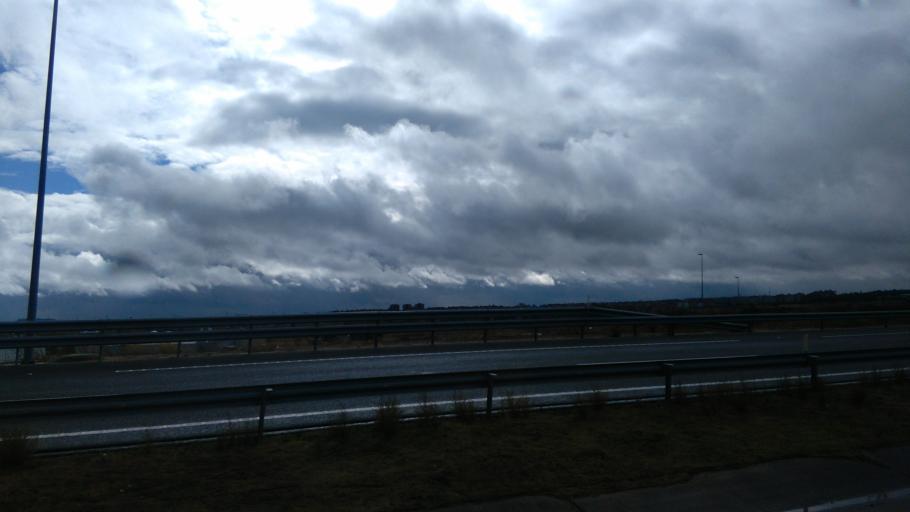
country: ES
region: Madrid
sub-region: Provincia de Madrid
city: Leganes
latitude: 40.3575
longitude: -3.7528
